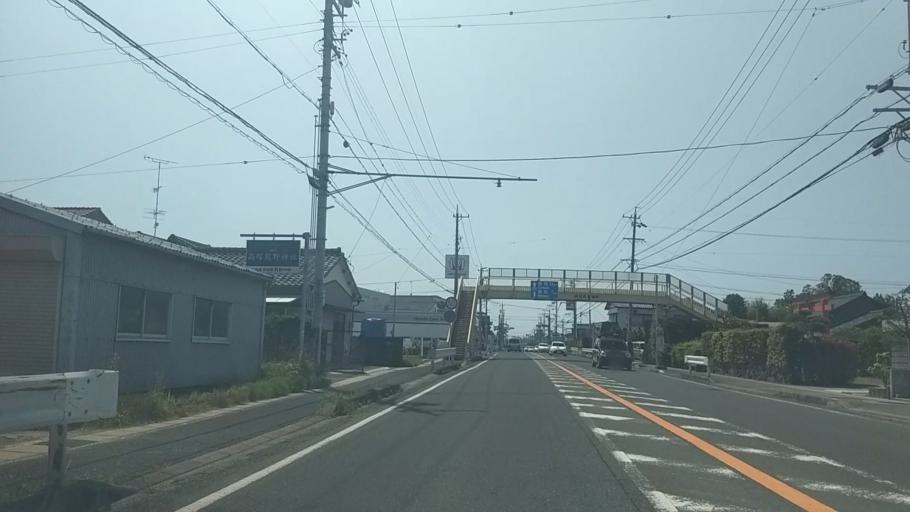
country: JP
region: Shizuoka
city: Hamamatsu
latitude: 34.6878
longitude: 137.6814
